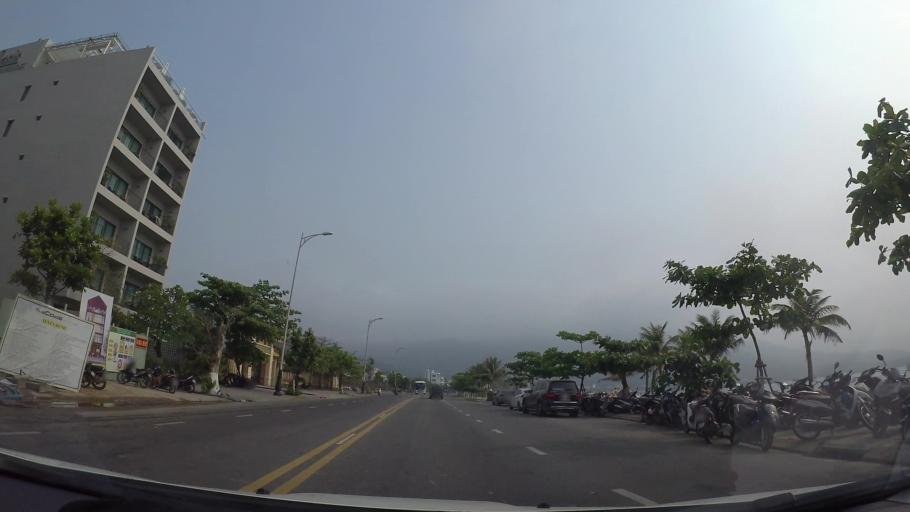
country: VN
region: Da Nang
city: Son Tra
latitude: 16.0953
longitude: 108.2523
